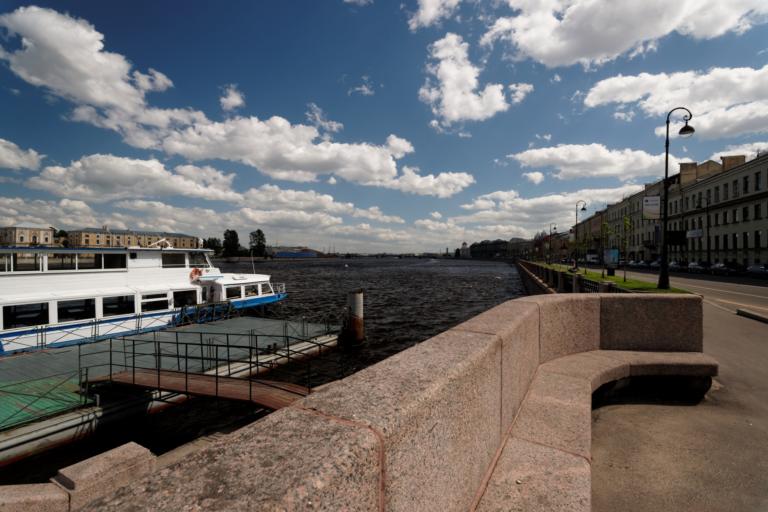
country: RU
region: St.-Petersburg
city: Saint Petersburg
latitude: 59.9474
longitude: 30.2862
